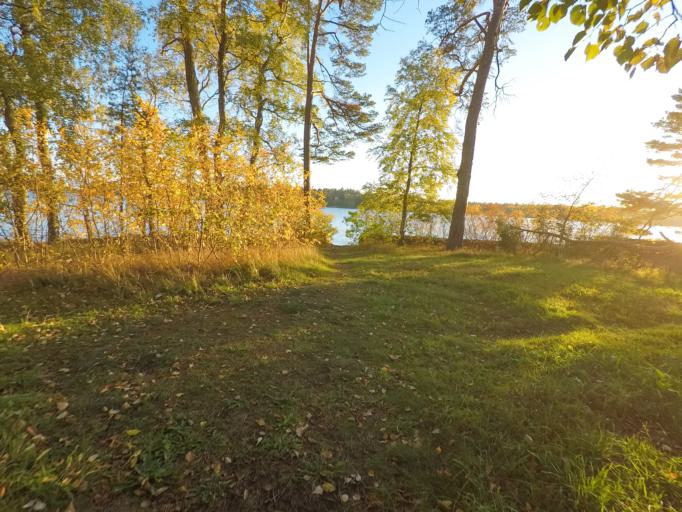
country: FI
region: Uusimaa
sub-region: Helsinki
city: Vantaa
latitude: 60.1551
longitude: 25.0813
